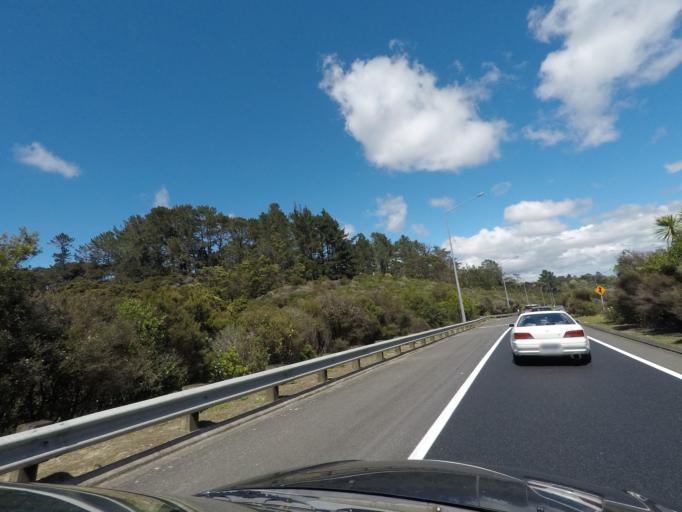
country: NZ
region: Auckland
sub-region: Auckland
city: Rothesay Bay
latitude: -36.7602
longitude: 174.7015
